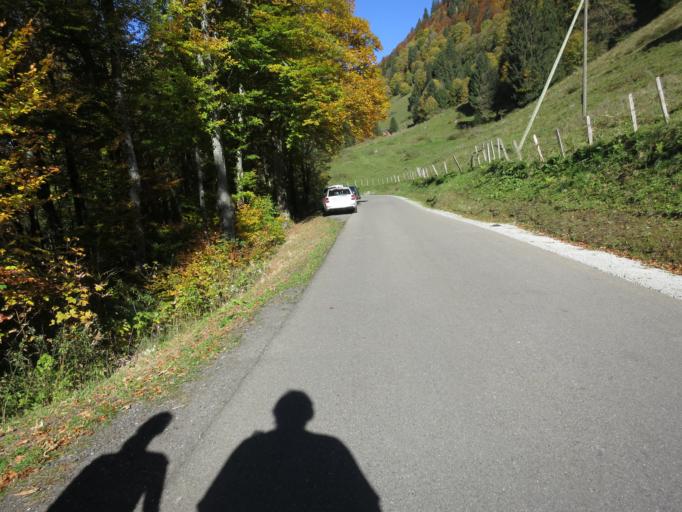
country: CH
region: Schwyz
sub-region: Bezirk March
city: Vorderthal
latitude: 47.0839
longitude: 8.9298
